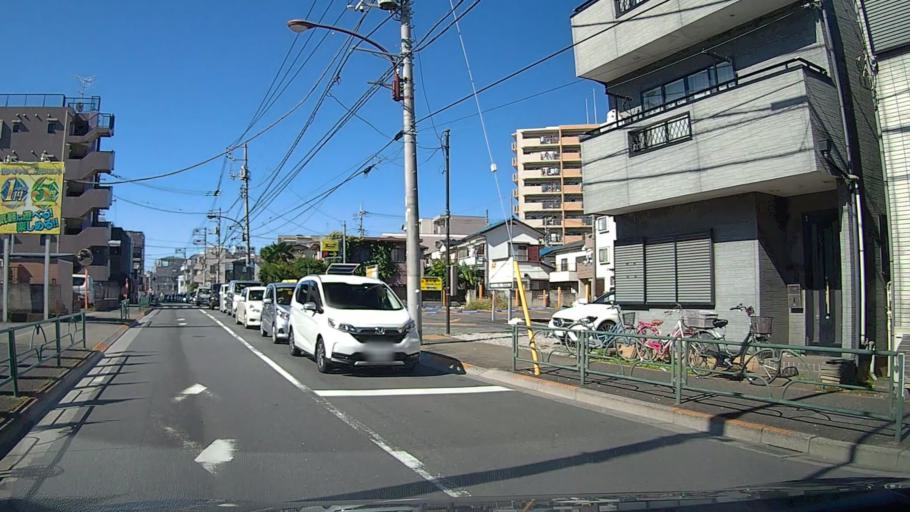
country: JP
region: Saitama
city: Wako
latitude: 35.7667
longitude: 139.6196
